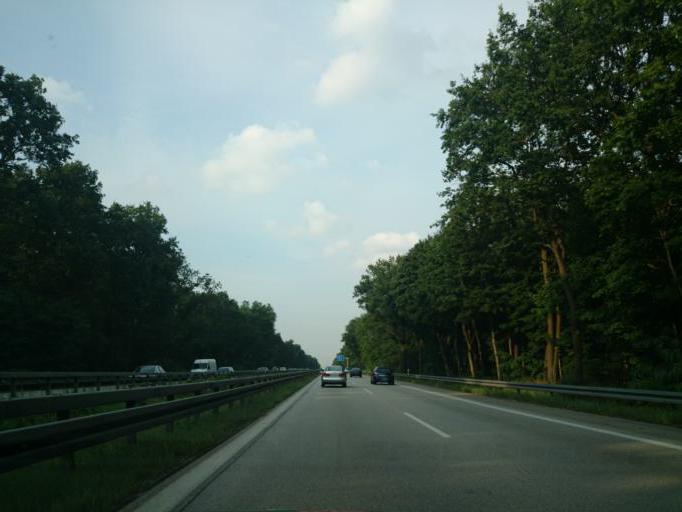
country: DE
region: Berlin
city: Nikolassee
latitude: 52.4573
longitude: 13.2217
